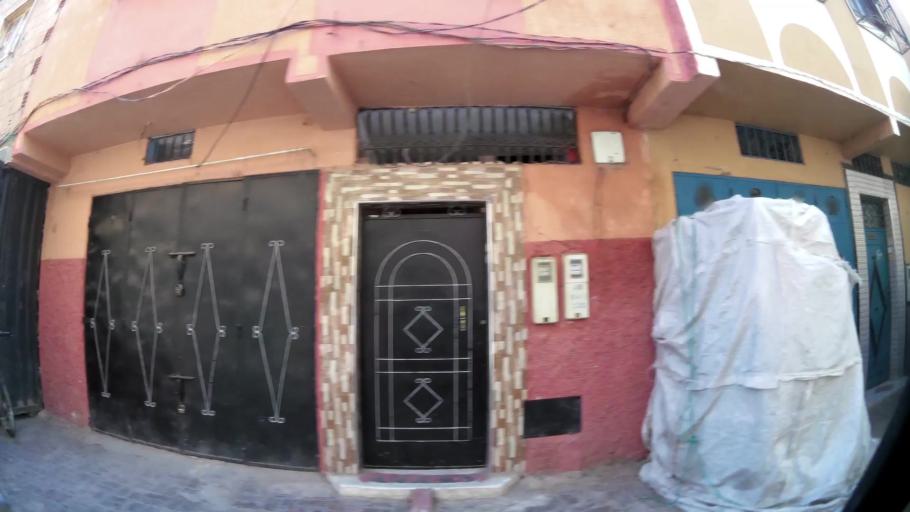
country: MA
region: Marrakech-Tensift-Al Haouz
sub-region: Marrakech
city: Marrakesh
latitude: 31.6637
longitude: -7.9854
